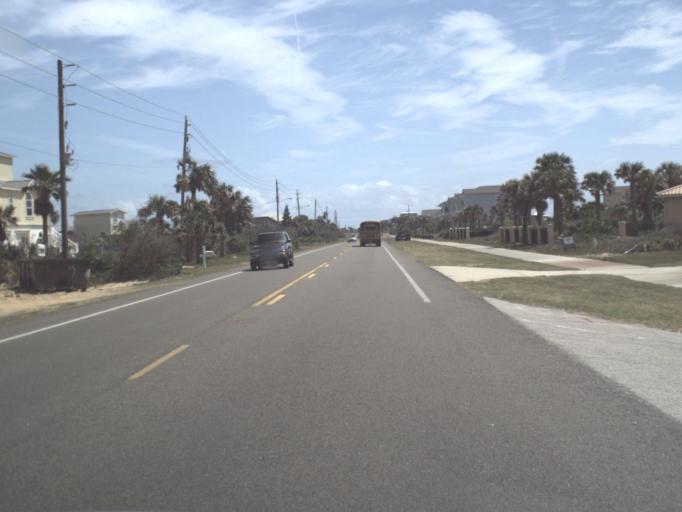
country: US
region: Florida
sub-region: Flagler County
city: Flagler Beach
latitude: 29.5189
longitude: -81.1465
